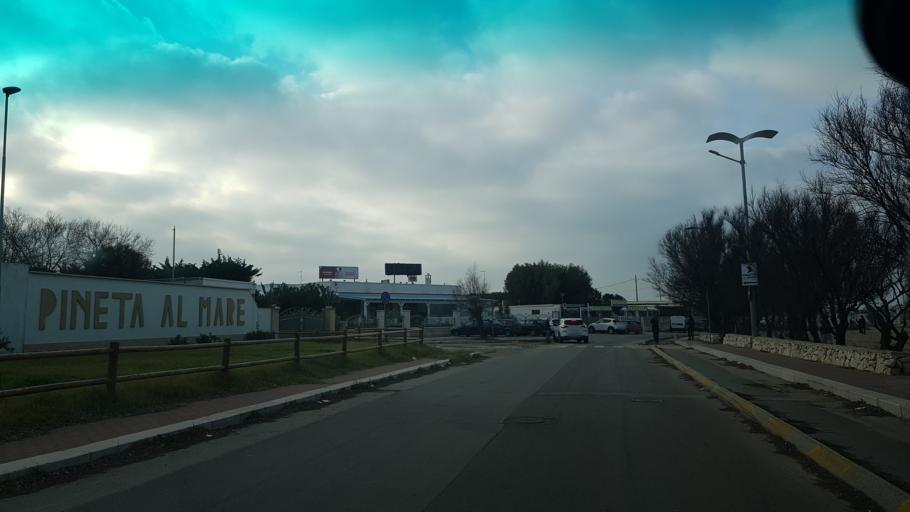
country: IT
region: Apulia
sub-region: Provincia di Brindisi
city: Carovigno
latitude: 40.7409
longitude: 17.7369
